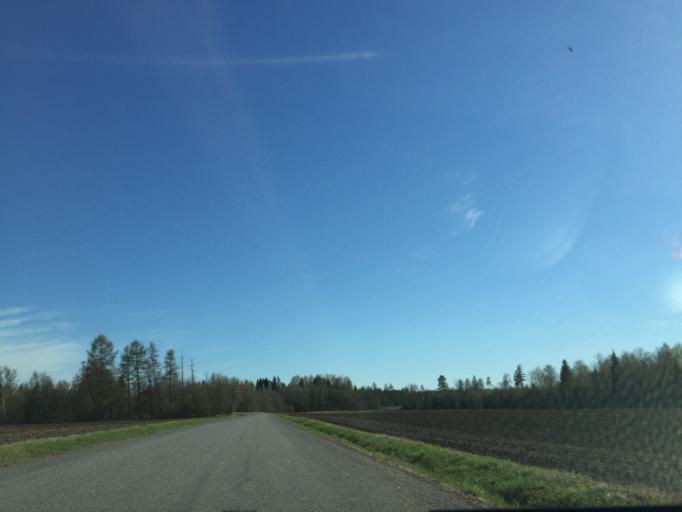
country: EE
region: Valgamaa
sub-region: Valga linn
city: Valga
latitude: 57.8535
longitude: 26.2534
